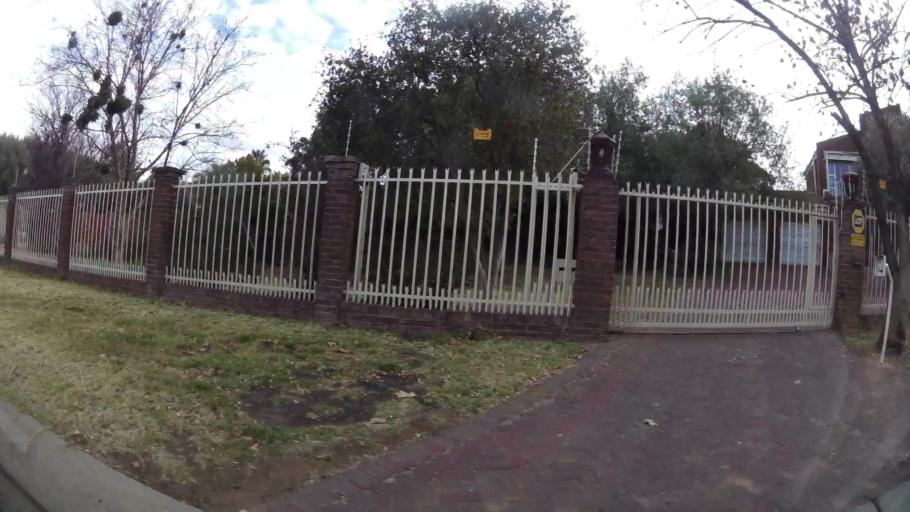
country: ZA
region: Orange Free State
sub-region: Mangaung Metropolitan Municipality
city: Bloemfontein
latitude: -29.0797
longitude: 26.2034
